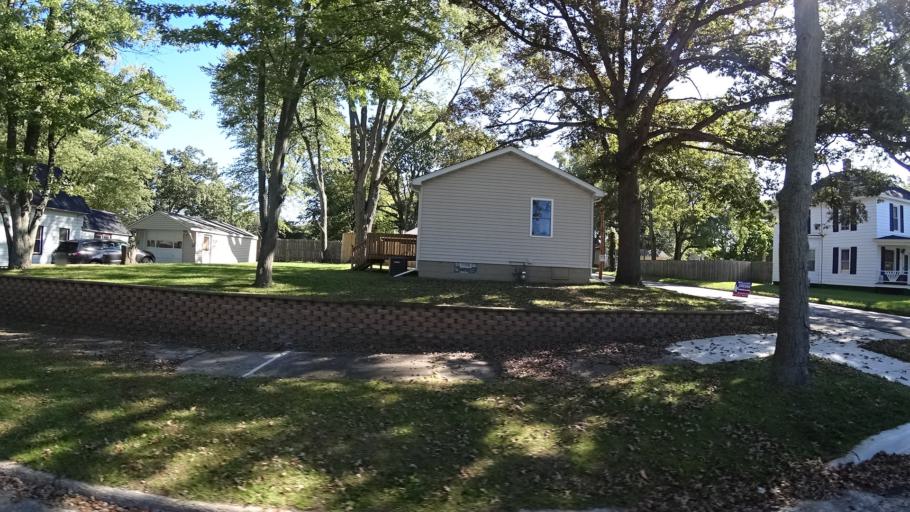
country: US
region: Indiana
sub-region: LaPorte County
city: Michigan City
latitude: 41.7060
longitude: -86.8807
